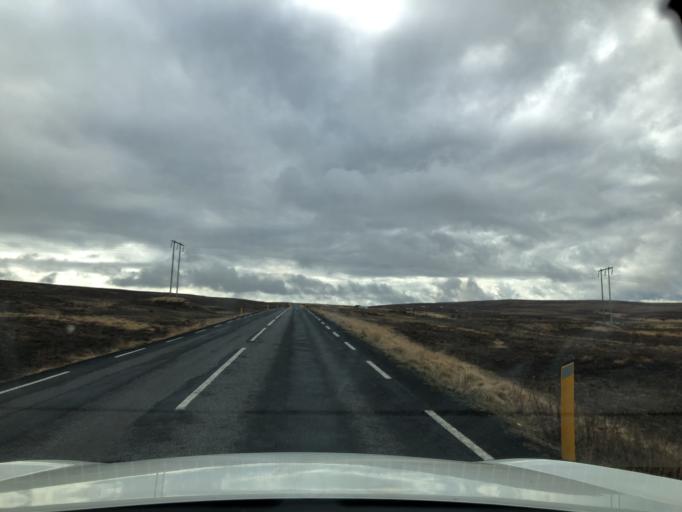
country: IS
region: Northeast
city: Laugar
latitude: 65.6574
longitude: -17.2836
